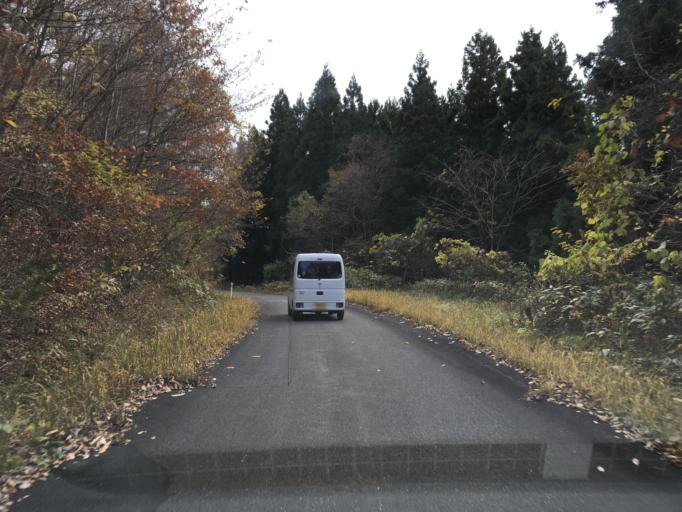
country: JP
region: Iwate
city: Mizusawa
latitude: 39.1258
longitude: 141.3183
